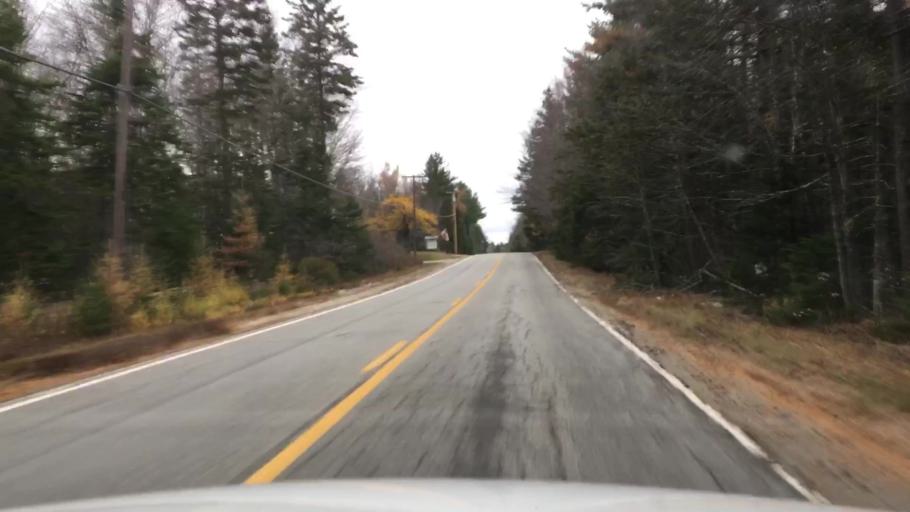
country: US
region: Maine
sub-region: Hancock County
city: Sedgwick
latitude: 44.2818
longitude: -68.5542
